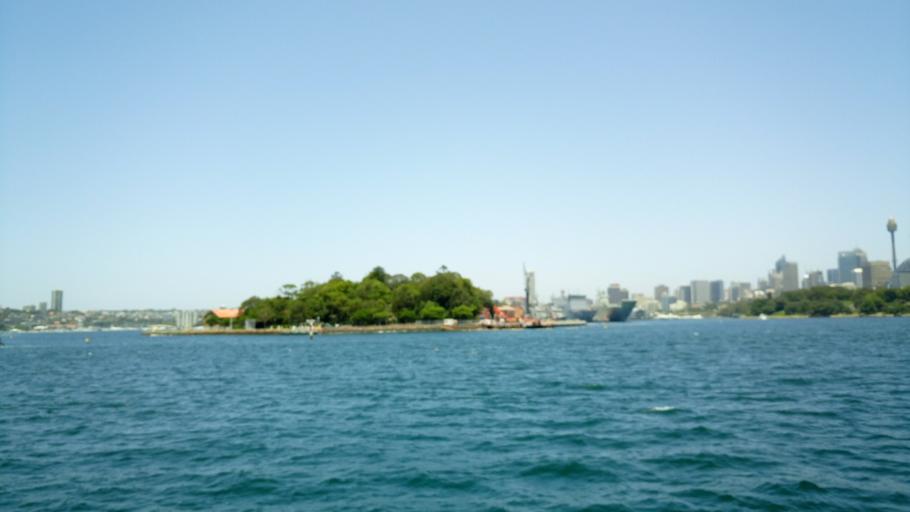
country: AU
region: New South Wales
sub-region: North Sydney
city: Kurraba Point
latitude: -33.8547
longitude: 151.2303
